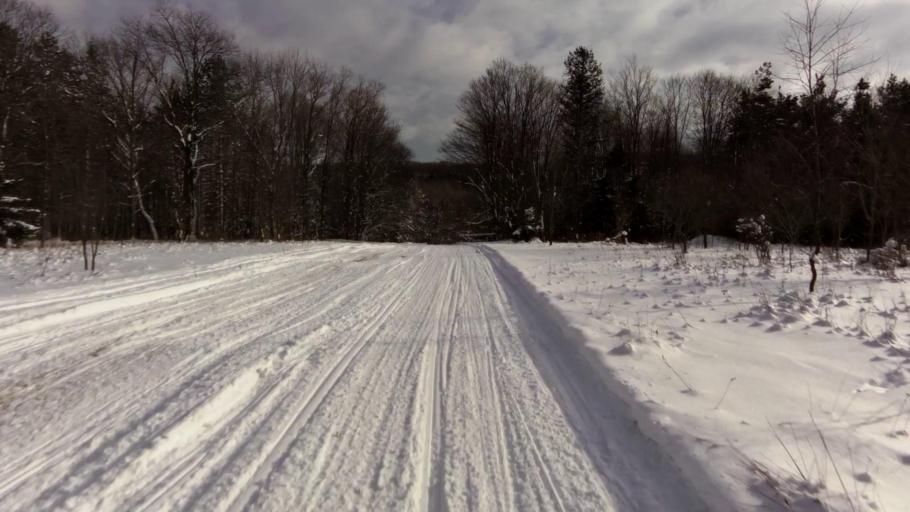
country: US
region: New York
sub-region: Cattaraugus County
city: Franklinville
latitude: 42.2996
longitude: -78.5189
